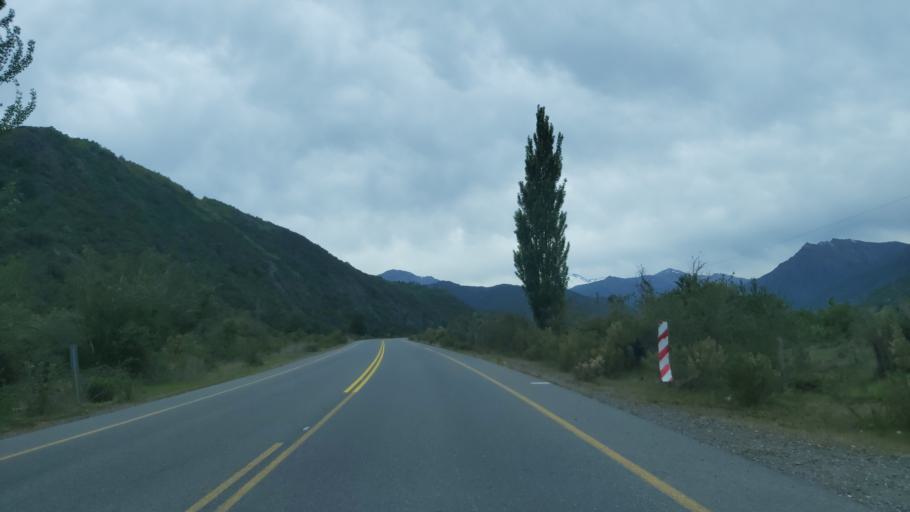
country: CL
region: Maule
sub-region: Provincia de Linares
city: Colbun
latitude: -35.7321
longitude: -71.0140
